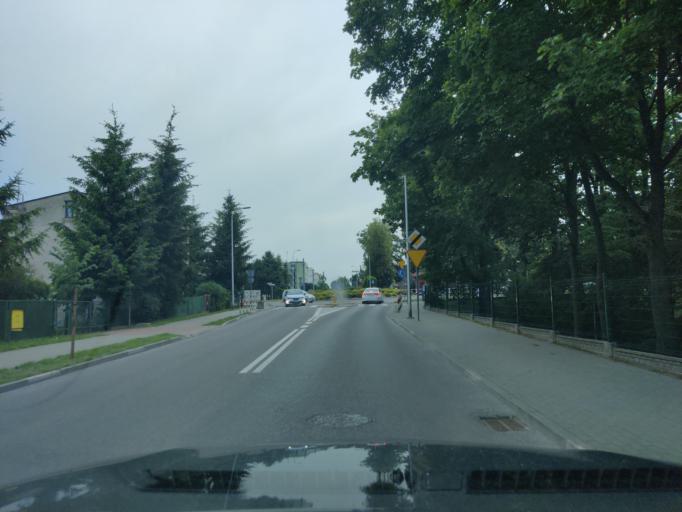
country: PL
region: Warmian-Masurian Voivodeship
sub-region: Powiat dzialdowski
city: Dzialdowo
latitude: 53.2379
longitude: 20.1859
